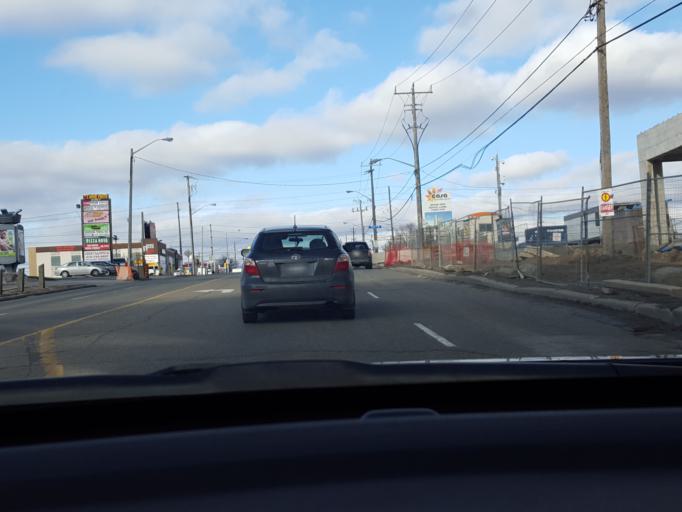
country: CA
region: Ontario
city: Concord
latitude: 43.7503
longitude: -79.5419
